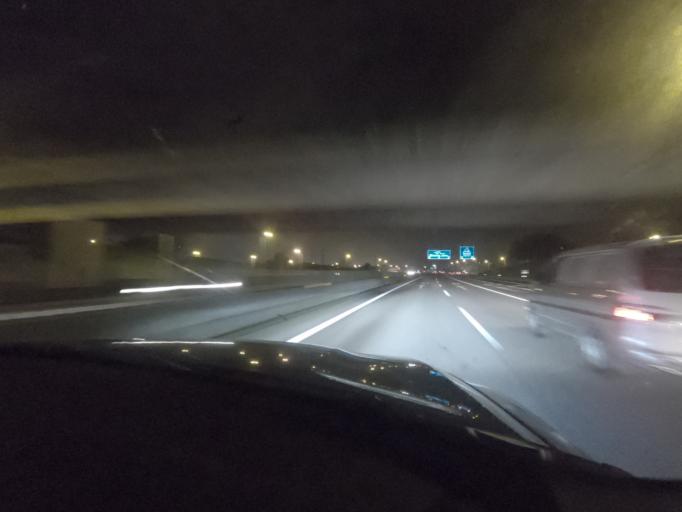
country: PT
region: Lisbon
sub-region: Alenquer
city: Carregado
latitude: 39.0249
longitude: -8.9631
